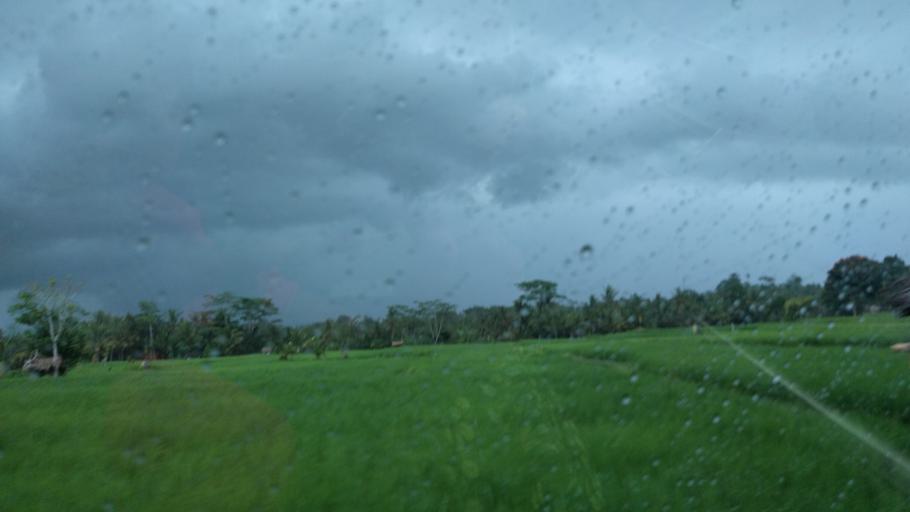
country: ID
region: Bali
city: Bunutan
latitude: -8.4803
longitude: 115.2583
